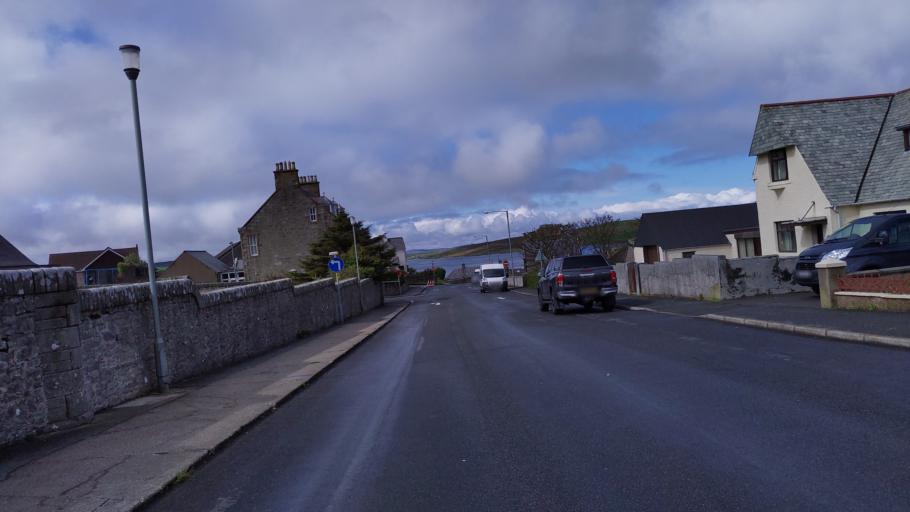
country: GB
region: Scotland
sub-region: Shetland Islands
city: Shetland
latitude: 60.1505
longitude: -1.1353
